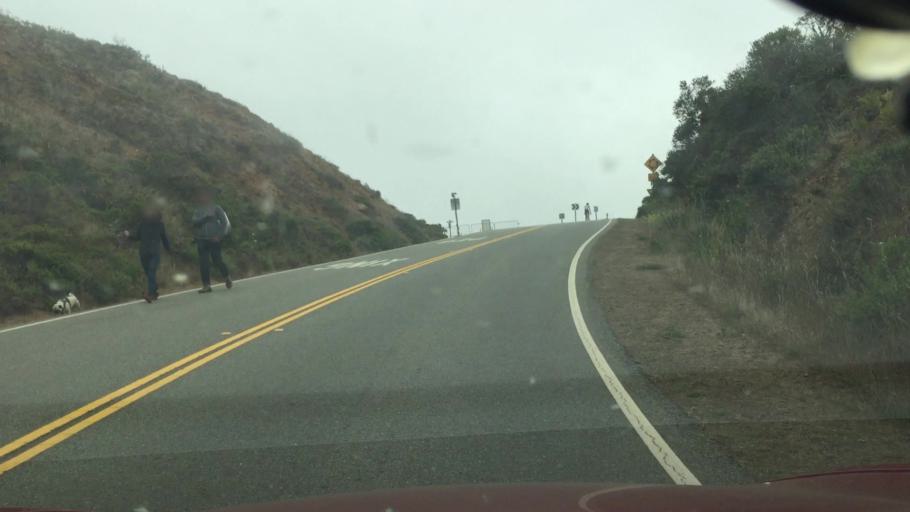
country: US
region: California
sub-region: Marin County
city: Sausalito
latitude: 37.8345
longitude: -122.4943
